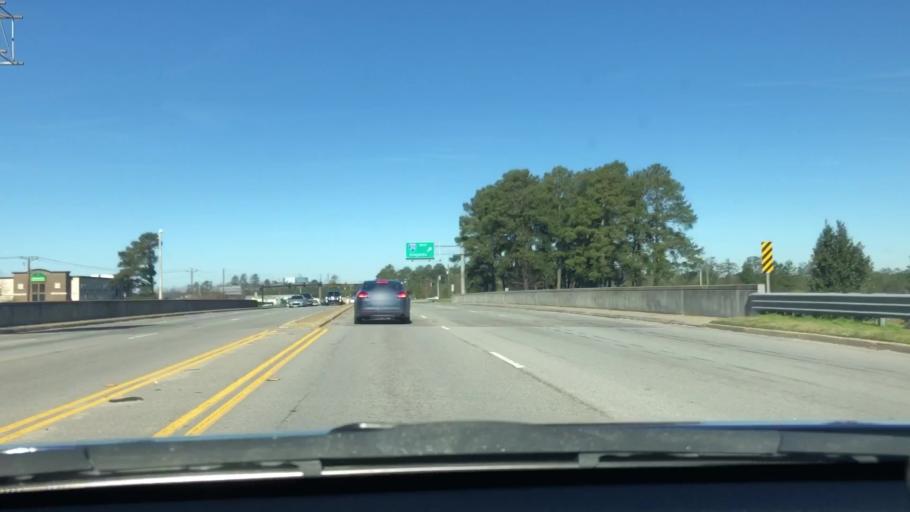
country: US
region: South Carolina
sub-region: Lexington County
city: Oak Grove
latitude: 34.0109
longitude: -81.1483
